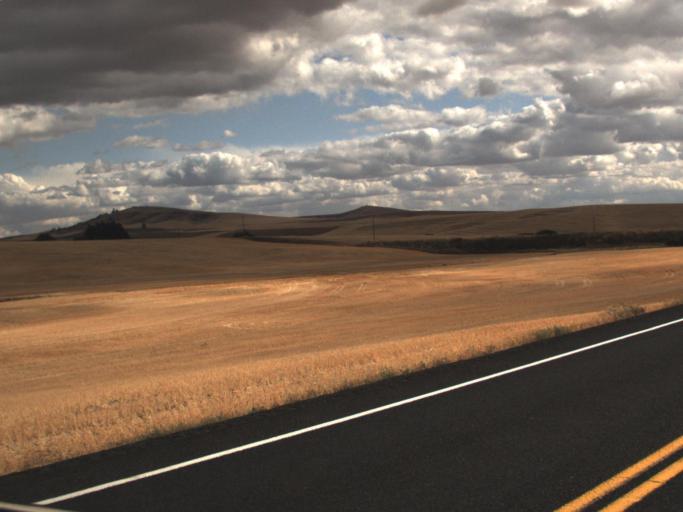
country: US
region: Washington
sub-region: Lincoln County
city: Davenport
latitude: 47.6164
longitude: -117.9376
